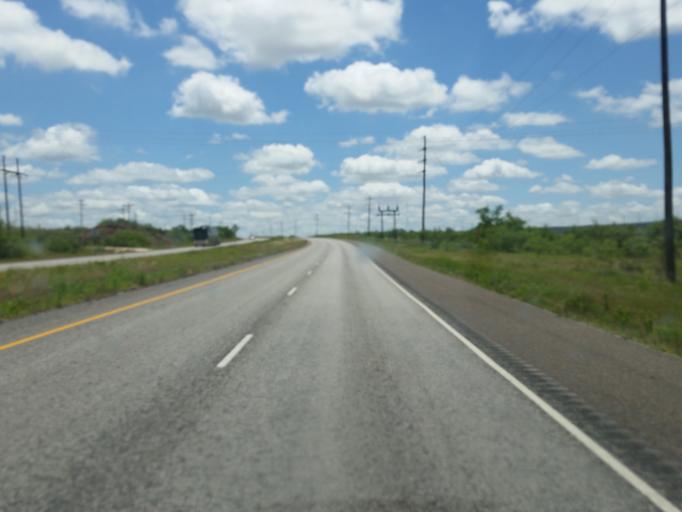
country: US
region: Texas
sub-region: Garza County
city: Post
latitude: 33.0037
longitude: -101.1640
